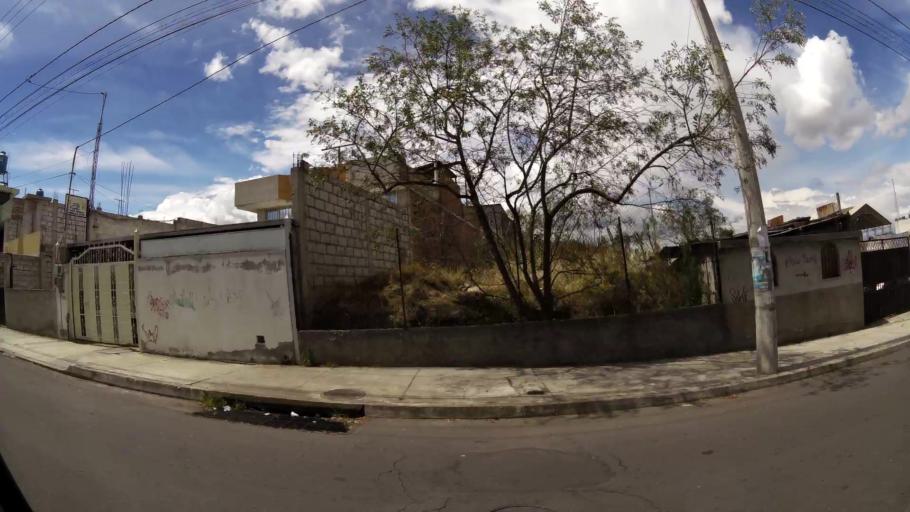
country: EC
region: Tungurahua
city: Ambato
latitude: -1.2639
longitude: -78.6211
